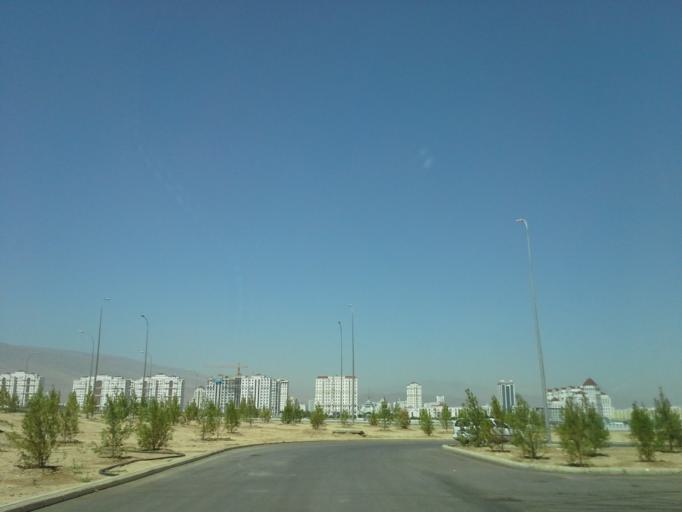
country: TM
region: Ahal
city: Ashgabat
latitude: 37.8906
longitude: 58.4066
